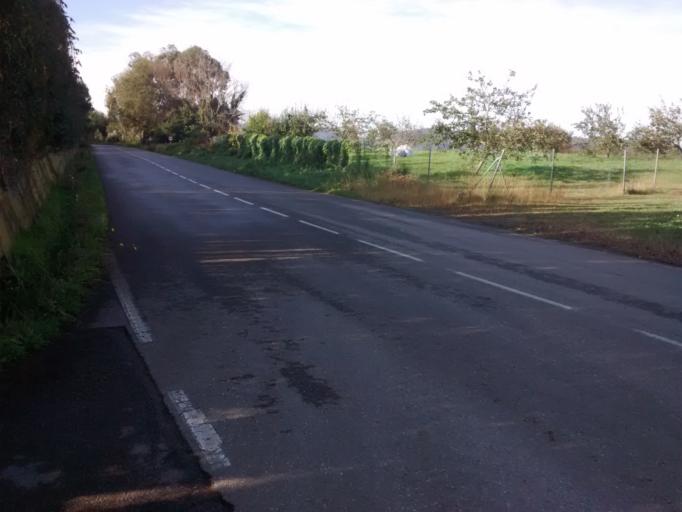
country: ES
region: Asturias
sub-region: Province of Asturias
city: Colunga
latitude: 43.4723
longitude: -5.2391
